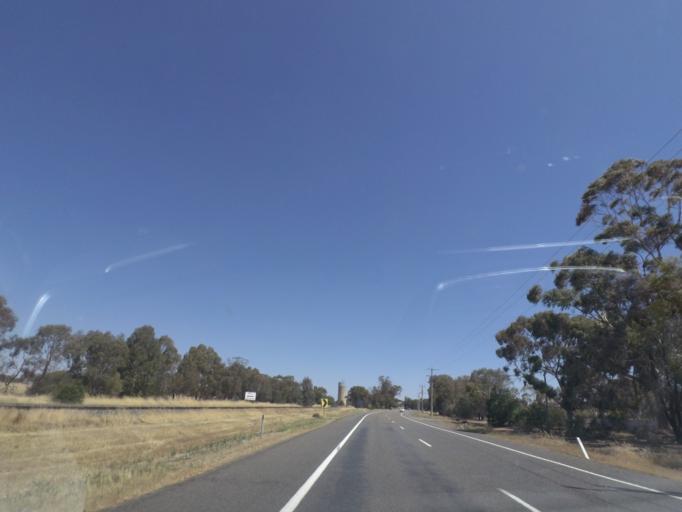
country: AU
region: Victoria
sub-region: Greater Shepparton
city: Shepparton
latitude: -36.2332
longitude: 145.4318
